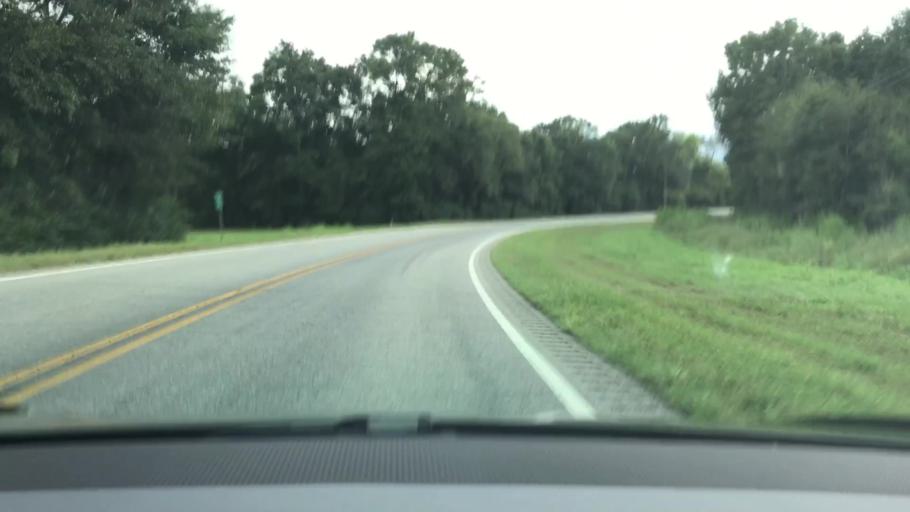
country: US
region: Alabama
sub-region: Coffee County
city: Elba
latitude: 31.5786
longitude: -85.9974
